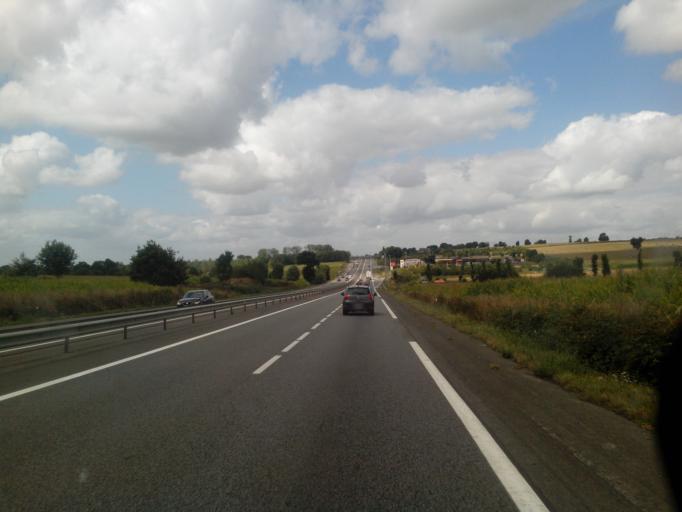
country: FR
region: Brittany
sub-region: Departement d'Ille-et-Vilaine
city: Saint-Gilles
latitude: 48.1635
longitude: -1.8611
